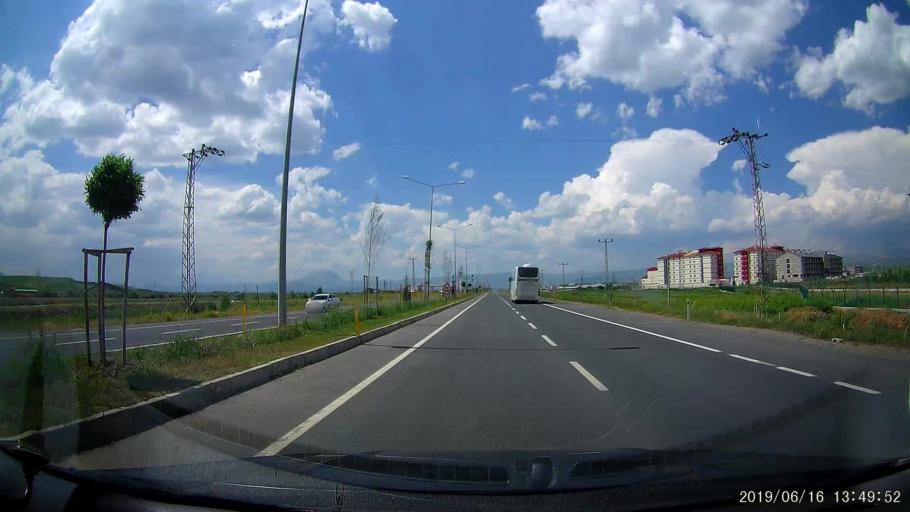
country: TR
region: Agri
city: Agri
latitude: 39.7211
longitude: 42.9857
